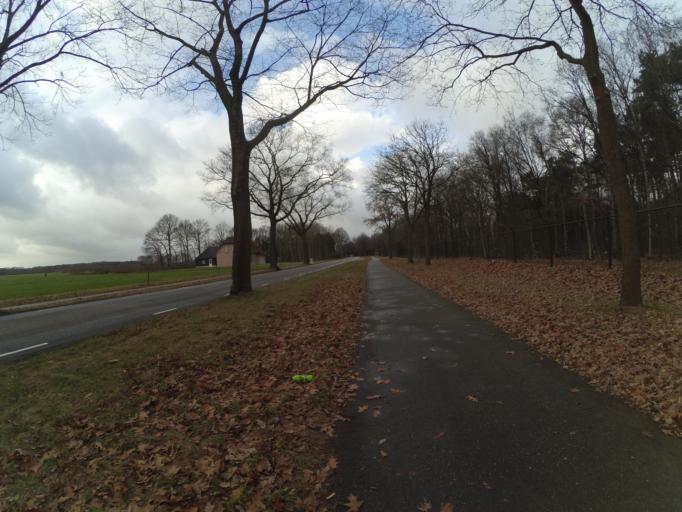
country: NL
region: North Brabant
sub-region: Gemeente Rucphen
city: Rucphen
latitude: 51.5247
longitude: 4.5692
